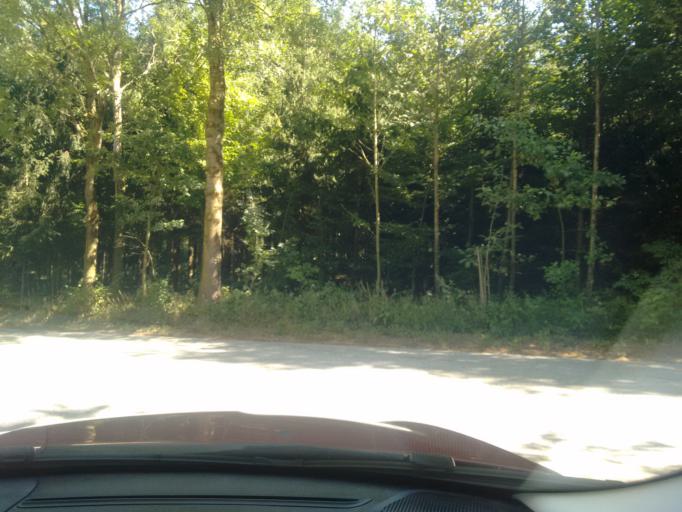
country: AT
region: Upper Austria
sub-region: Wels-Land
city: Steinhaus
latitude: 48.0988
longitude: 14.0459
